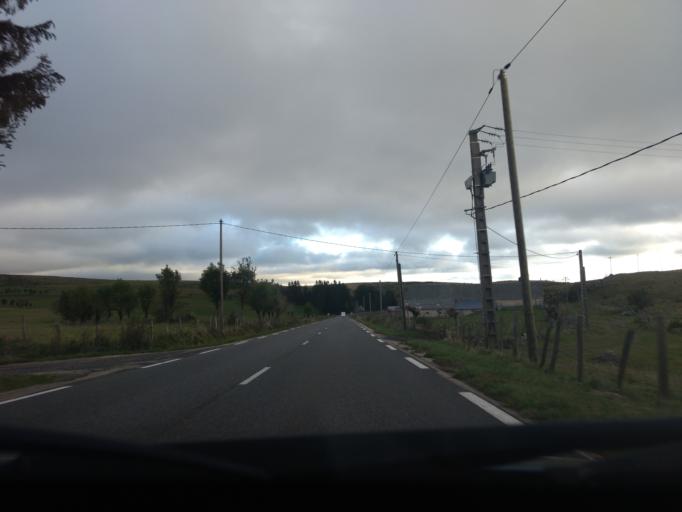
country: FR
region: Midi-Pyrenees
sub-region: Departement de l'Aveyron
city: Laguiole
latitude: 44.7246
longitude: 2.8698
